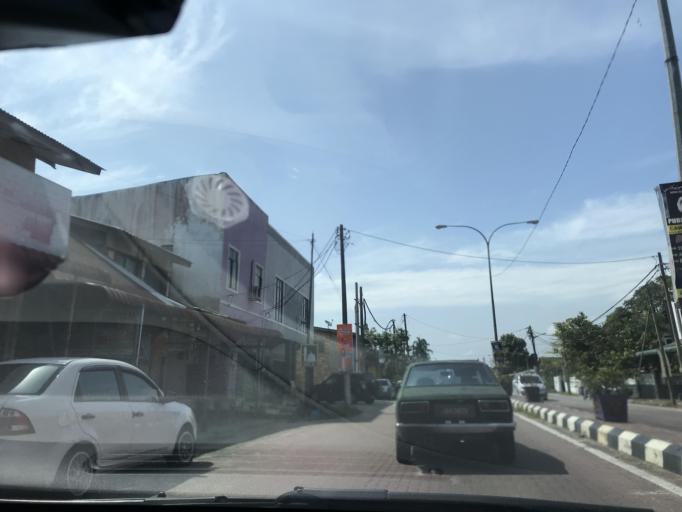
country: MY
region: Kelantan
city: Tumpat
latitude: 6.1525
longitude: 102.1571
